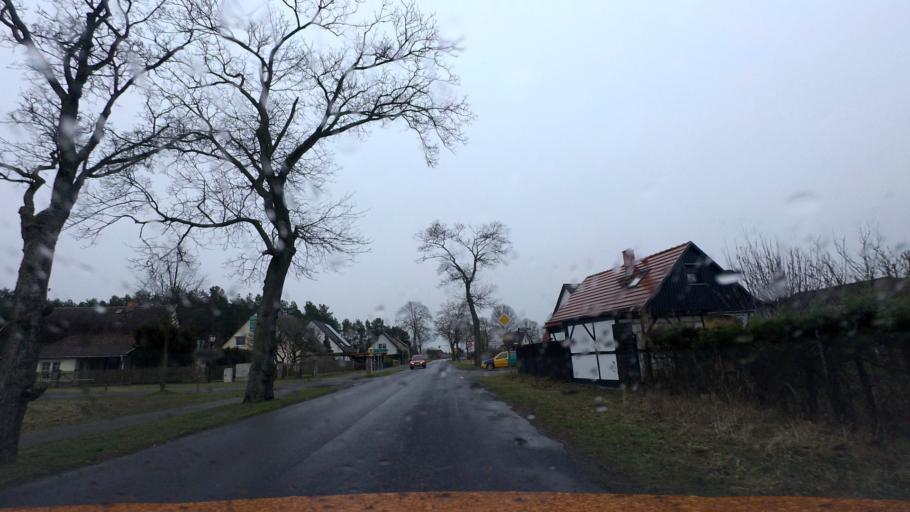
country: DE
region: Brandenburg
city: Brieselang
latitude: 52.6540
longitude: 12.9893
